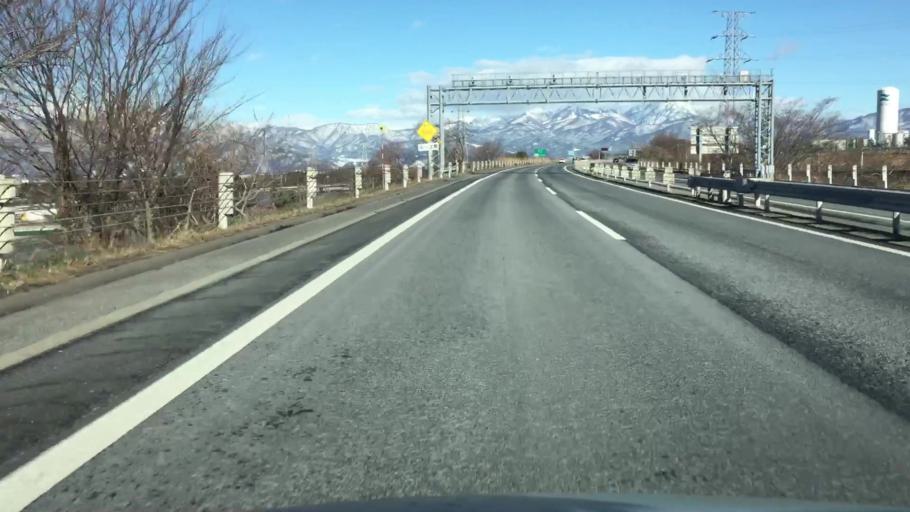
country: JP
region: Gunma
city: Numata
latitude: 36.6072
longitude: 139.0629
